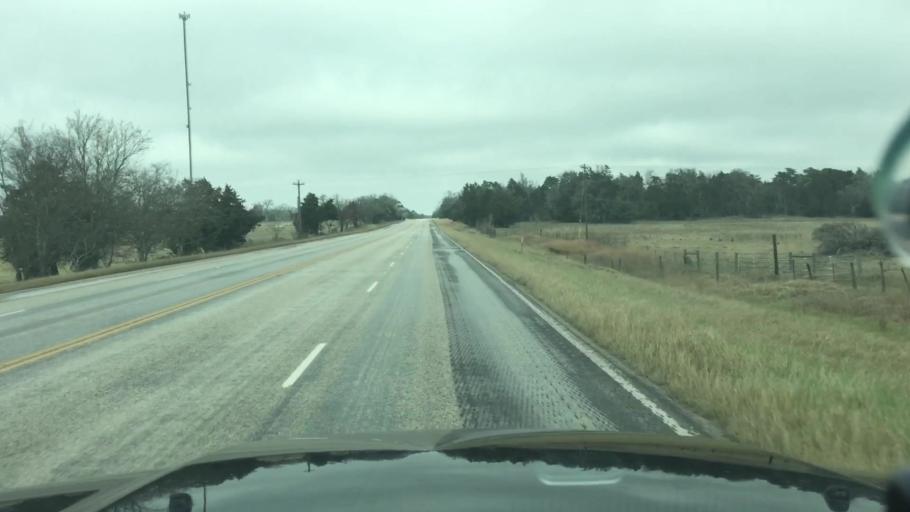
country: US
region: Texas
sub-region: Lee County
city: Giddings
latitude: 30.1058
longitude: -96.9144
